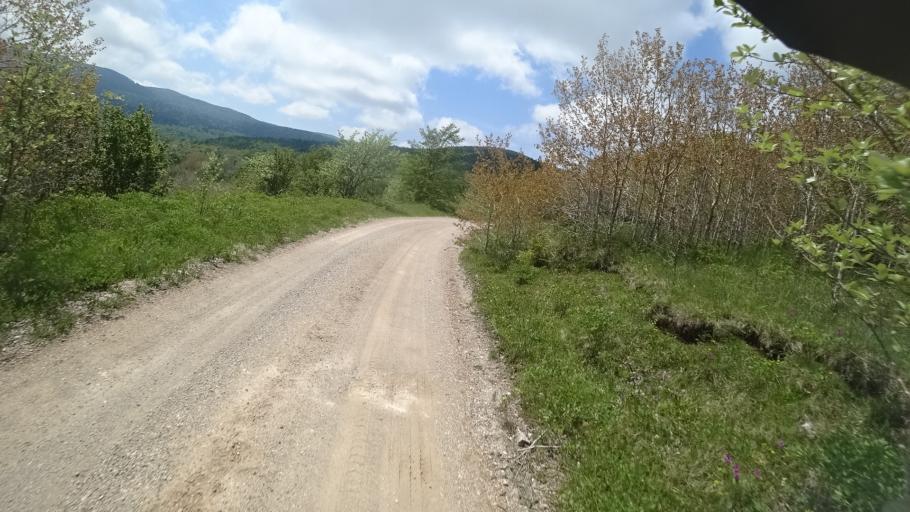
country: HR
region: Zadarska
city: Gracac
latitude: 44.5053
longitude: 15.8845
